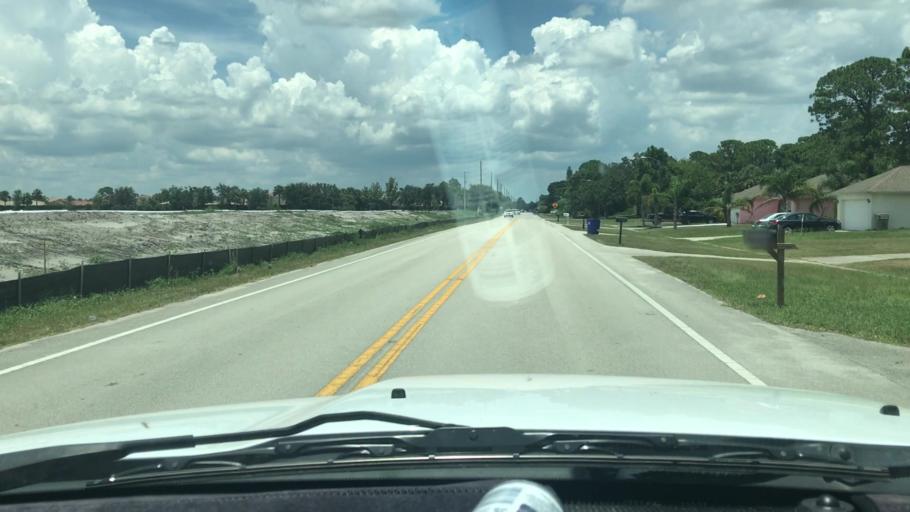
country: US
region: Florida
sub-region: Saint Lucie County
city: Lakewood Park
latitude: 27.5629
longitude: -80.4063
